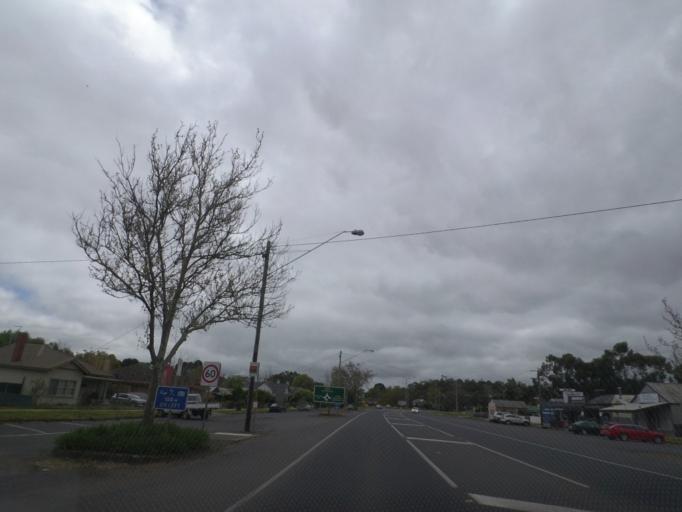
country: AU
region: Victoria
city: Brown Hill
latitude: -37.4206
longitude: 143.8946
